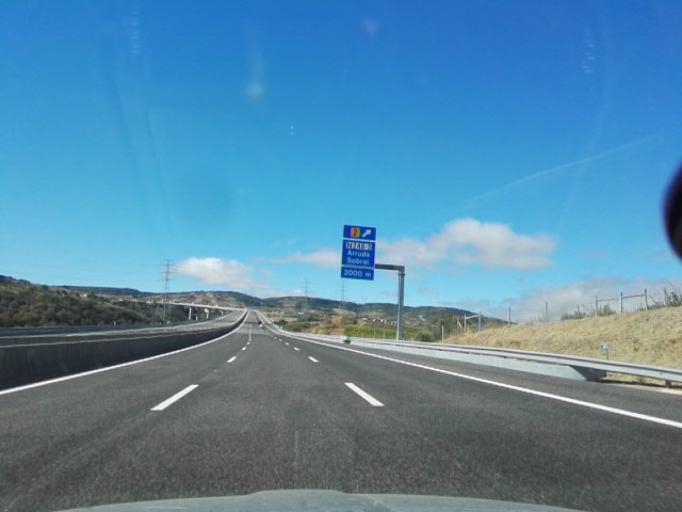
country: PT
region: Lisbon
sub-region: Arruda Dos Vinhos
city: Arruda dos Vinhos
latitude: 38.9860
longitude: -9.0505
